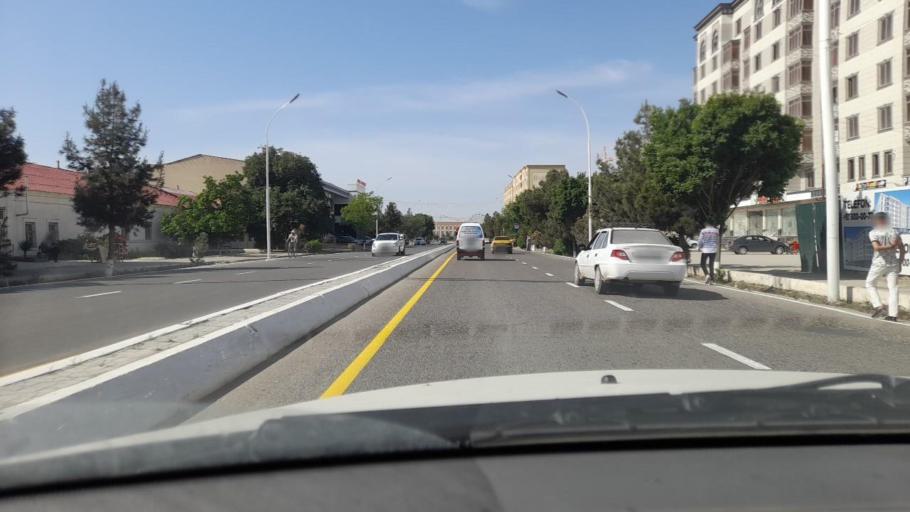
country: UZ
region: Bukhara
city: Bukhara
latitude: 39.7881
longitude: 64.4318
